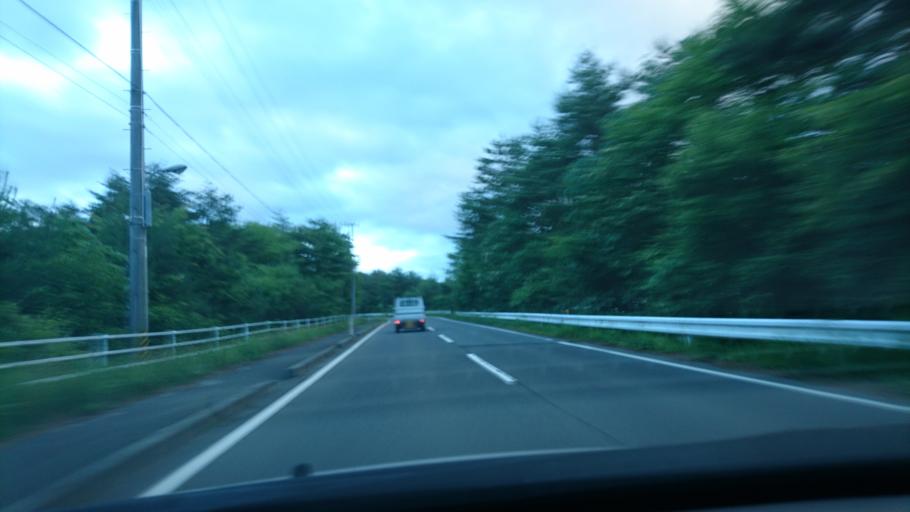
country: JP
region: Iwate
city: Ichinoseki
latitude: 38.7867
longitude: 141.0559
